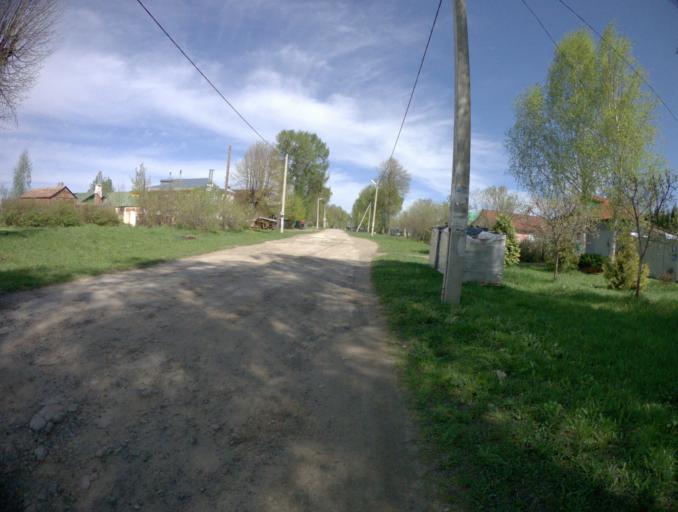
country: RU
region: Vladimir
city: Orgtrud
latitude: 56.2079
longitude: 40.5757
